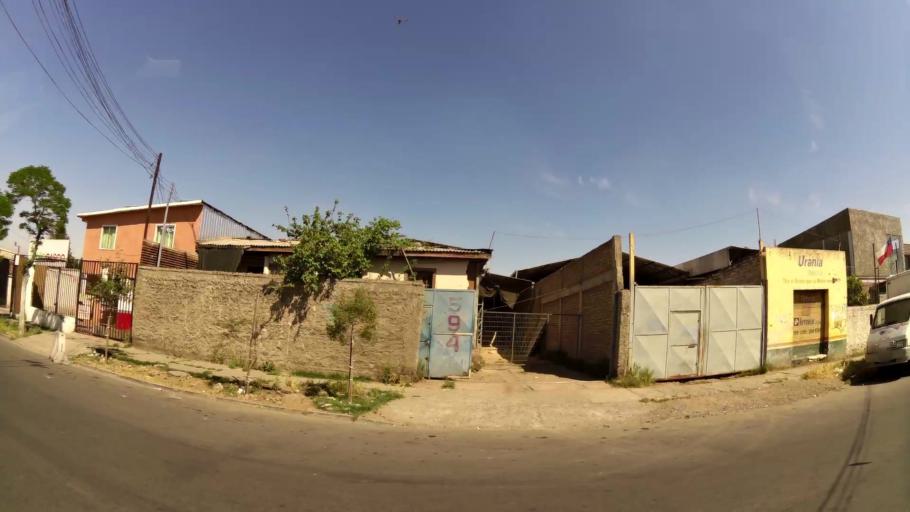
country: CL
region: Santiago Metropolitan
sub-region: Provincia de Santiago
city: Santiago
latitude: -33.5161
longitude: -70.6416
